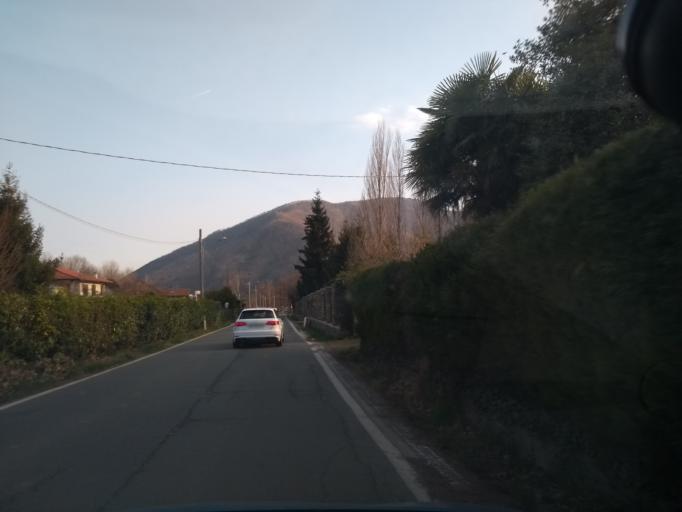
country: IT
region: Piedmont
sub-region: Provincia di Torino
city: Lanzo Torinese
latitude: 45.2790
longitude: 7.4845
